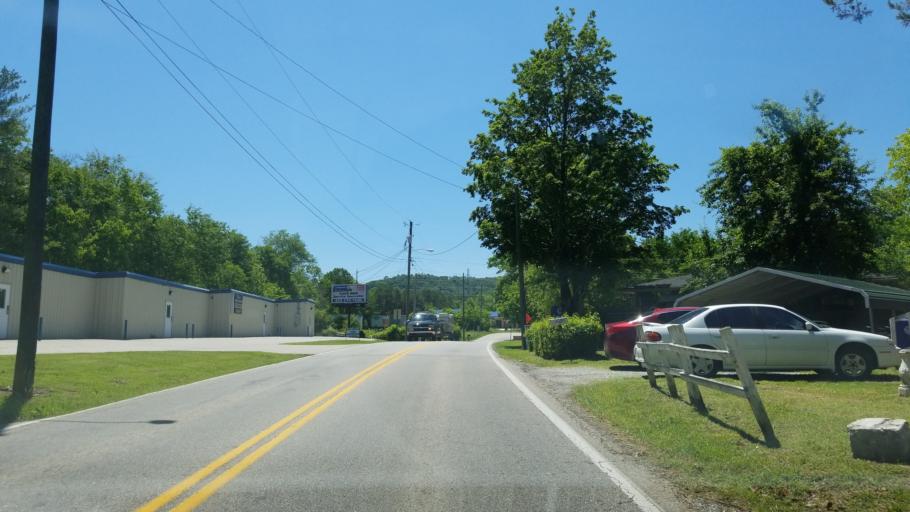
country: US
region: Tennessee
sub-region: Hamilton County
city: Collegedale
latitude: 35.0699
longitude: -85.0641
